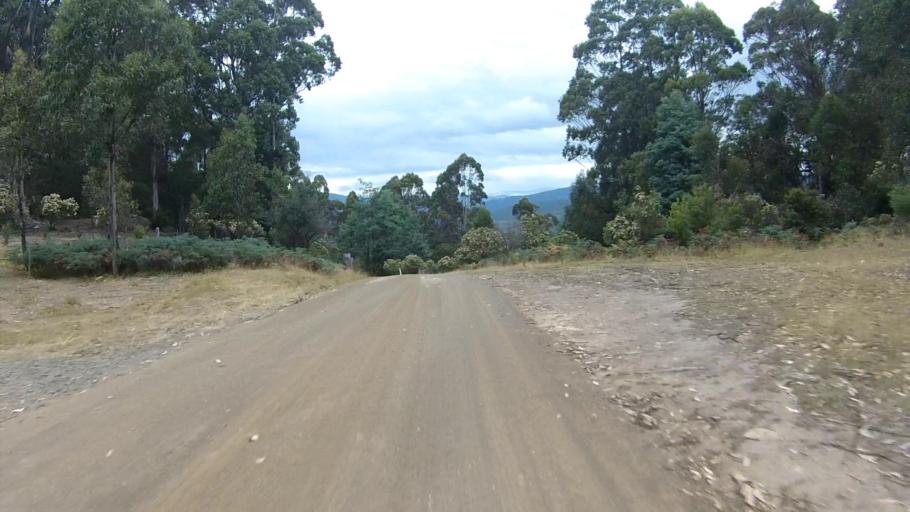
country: AU
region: Tasmania
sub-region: Huon Valley
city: Huonville
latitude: -42.9535
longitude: 147.0463
